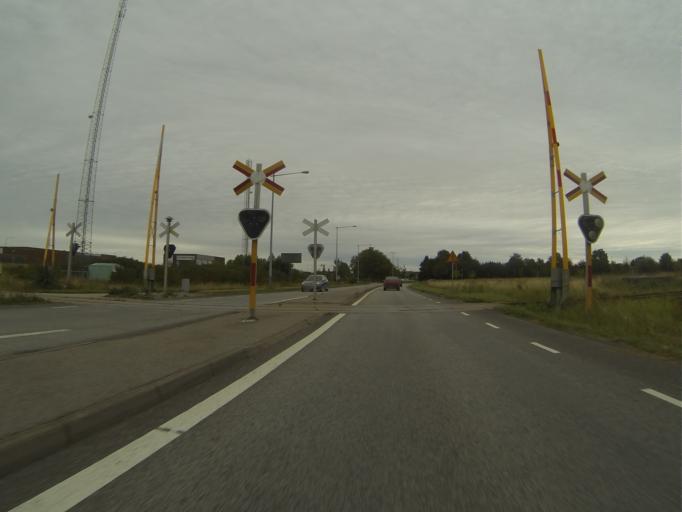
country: SE
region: Skane
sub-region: Staffanstorps Kommun
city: Staffanstorp
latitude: 55.6302
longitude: 13.1859
